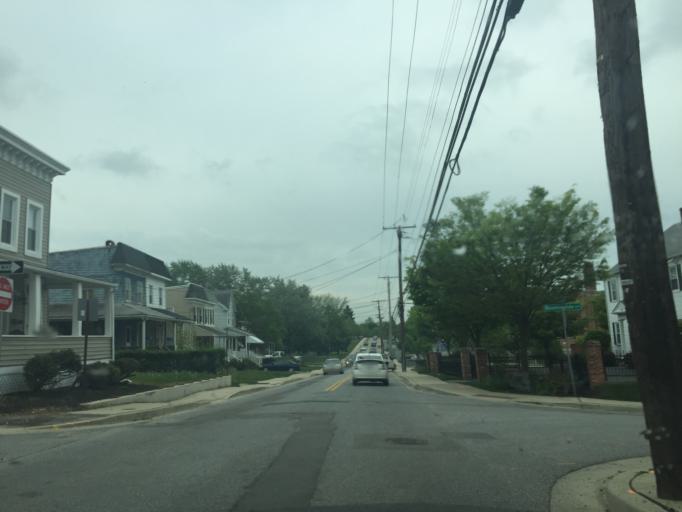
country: US
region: Maryland
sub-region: Baltimore County
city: Catonsville
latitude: 39.2697
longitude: -76.7307
